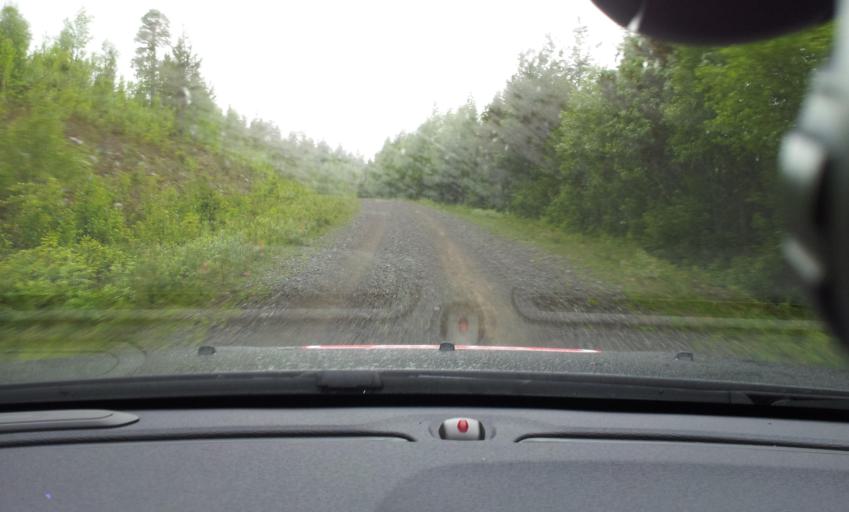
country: SE
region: Jaemtland
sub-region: Are Kommun
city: Jarpen
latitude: 63.1942
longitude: 13.3865
